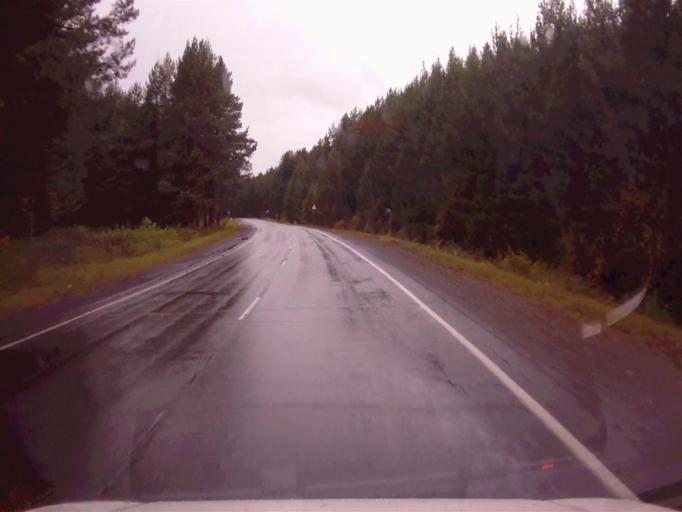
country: RU
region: Chelyabinsk
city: Verkhniy Ufaley
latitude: 56.0240
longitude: 60.2983
